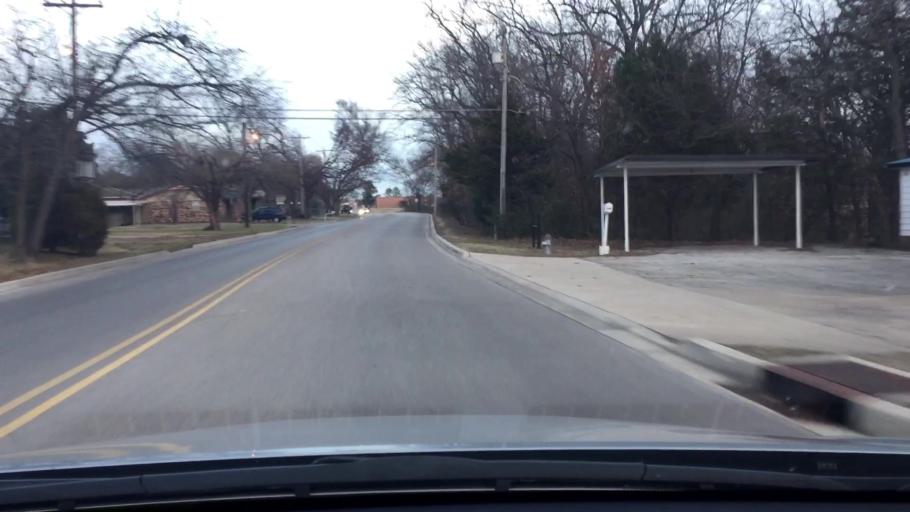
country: US
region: Oklahoma
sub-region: Carter County
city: Ardmore
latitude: 34.1802
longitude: -97.1521
